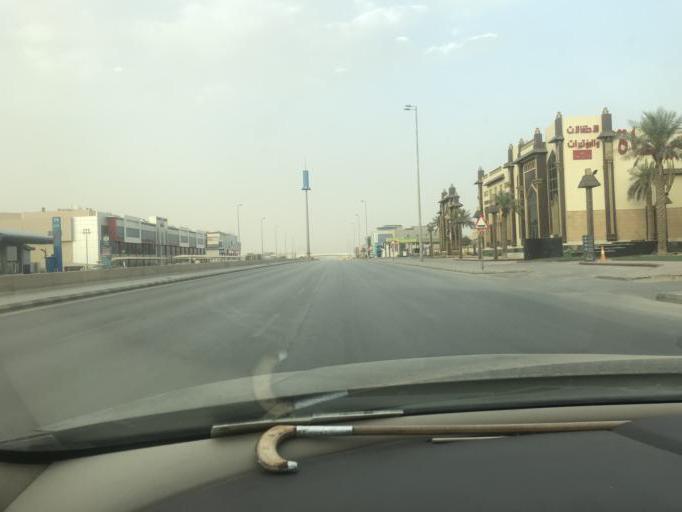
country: SA
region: Ar Riyad
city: Riyadh
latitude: 24.8072
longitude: 46.6628
